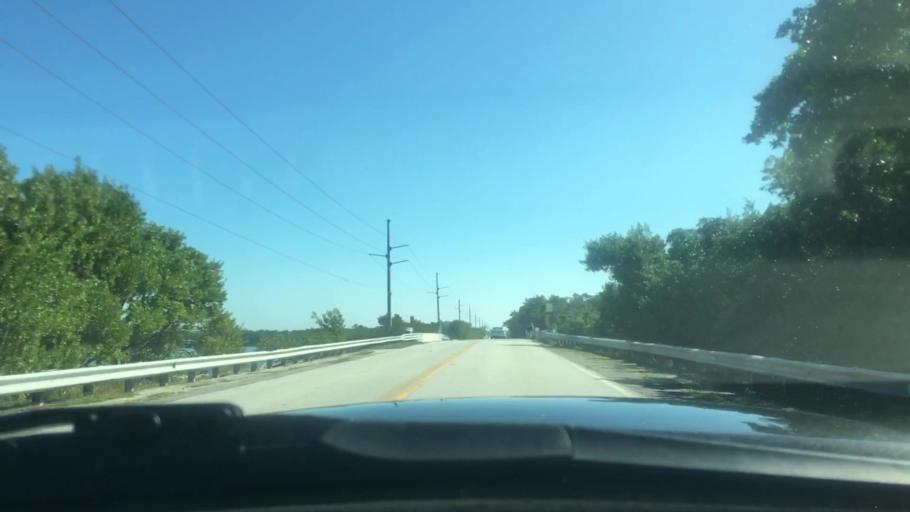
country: US
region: Florida
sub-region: Monroe County
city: North Key Largo
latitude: 25.2840
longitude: -80.3590
